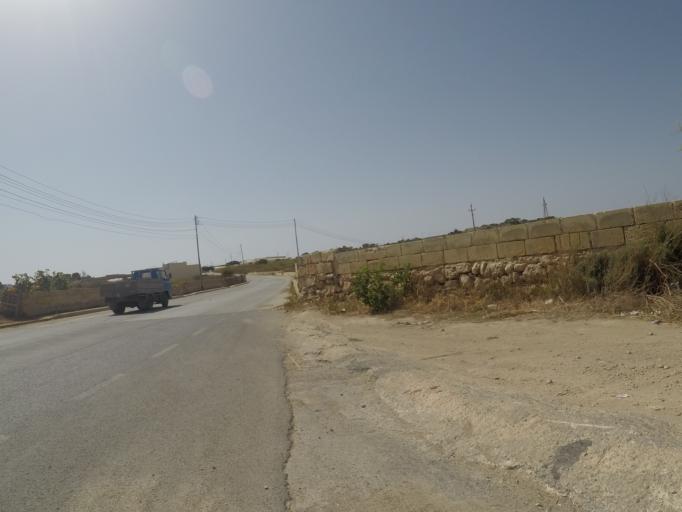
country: MT
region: L-Imgarr
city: Imgarr
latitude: 35.9236
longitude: 14.3771
